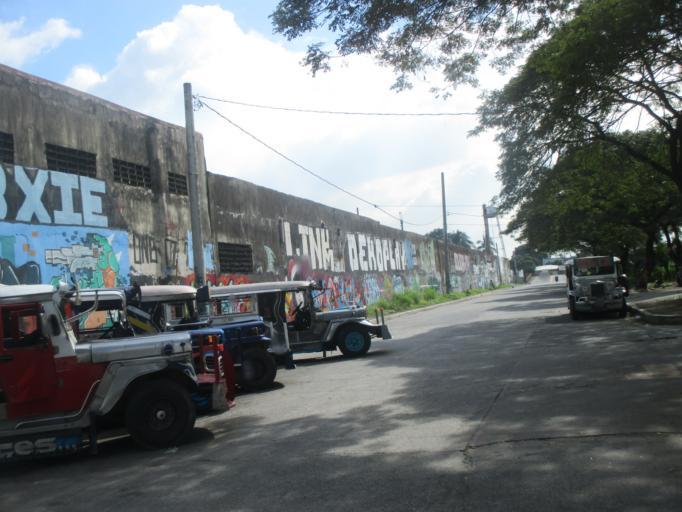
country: PH
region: Metro Manila
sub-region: Marikina
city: Calumpang
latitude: 14.6435
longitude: 121.1034
